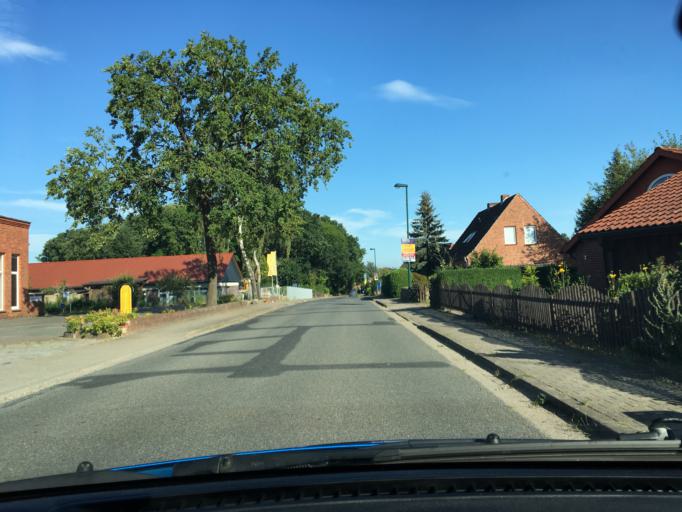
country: DE
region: Lower Saxony
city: Dahlenburg
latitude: 53.1899
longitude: 10.7298
